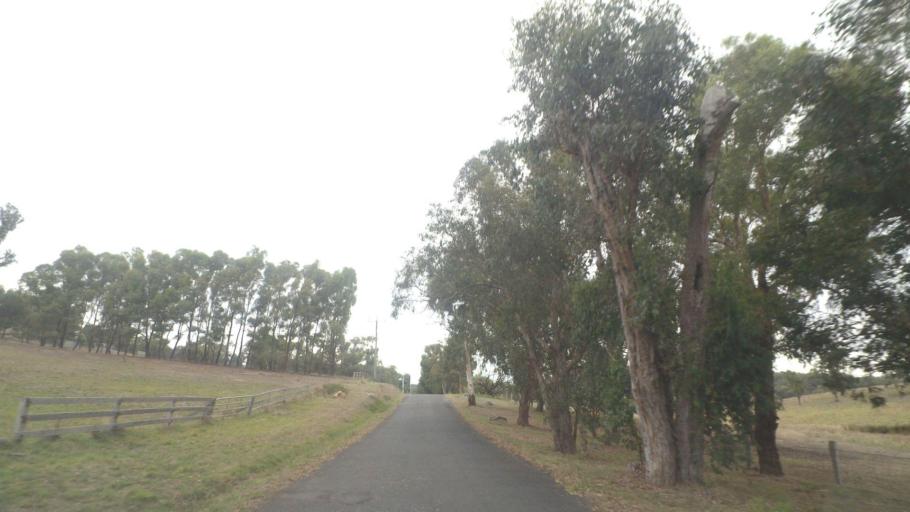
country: AU
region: Victoria
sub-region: Nillumbik
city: North Warrandyte
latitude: -37.7368
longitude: 145.1858
